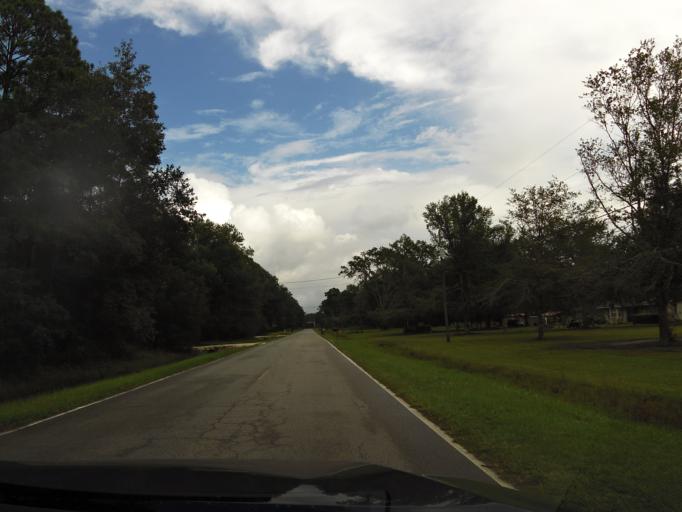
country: US
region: Florida
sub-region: Duval County
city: Baldwin
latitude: 30.3937
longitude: -81.9444
